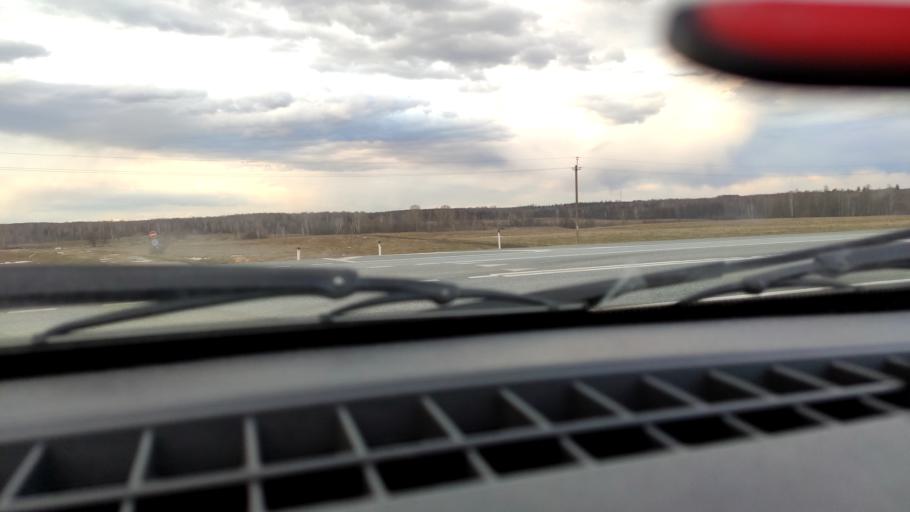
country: RU
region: Bashkortostan
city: Kudeyevskiy
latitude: 54.8168
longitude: 56.7576
